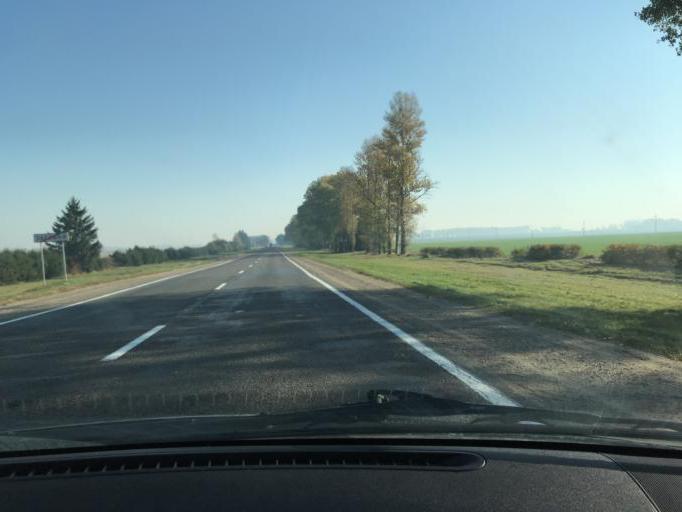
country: BY
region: Minsk
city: Klyetsk
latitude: 52.9713
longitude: 26.6738
